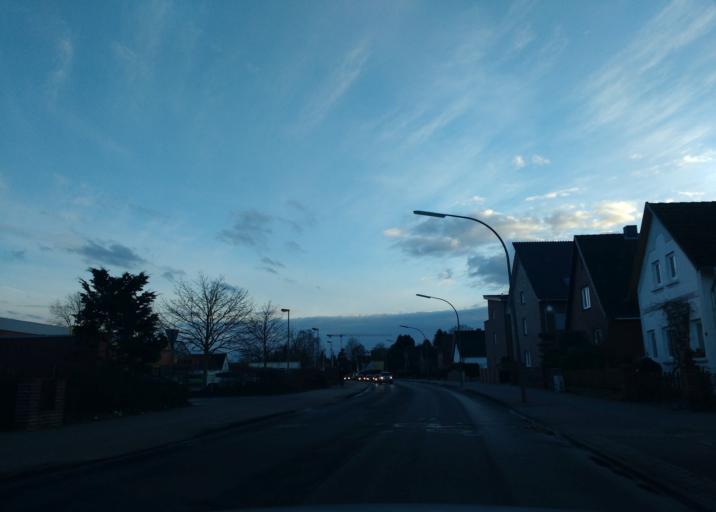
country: DE
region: Schleswig-Holstein
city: Norderstedt
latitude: 53.6730
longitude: 9.9871
